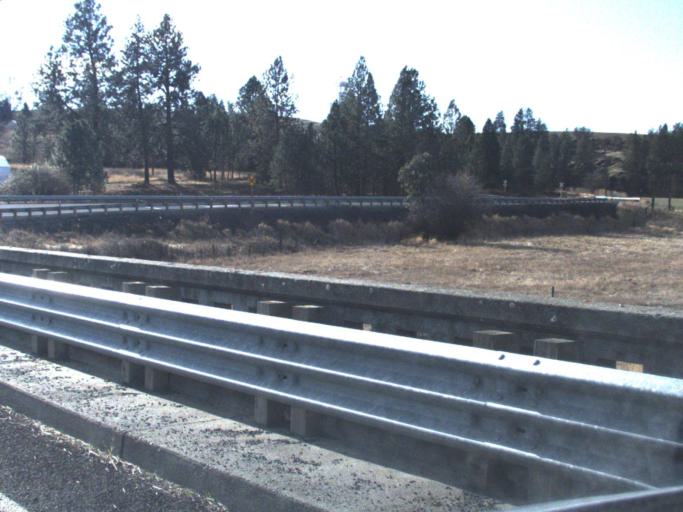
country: US
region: Idaho
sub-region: Latah County
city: Moscow
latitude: 46.9146
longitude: -117.0853
